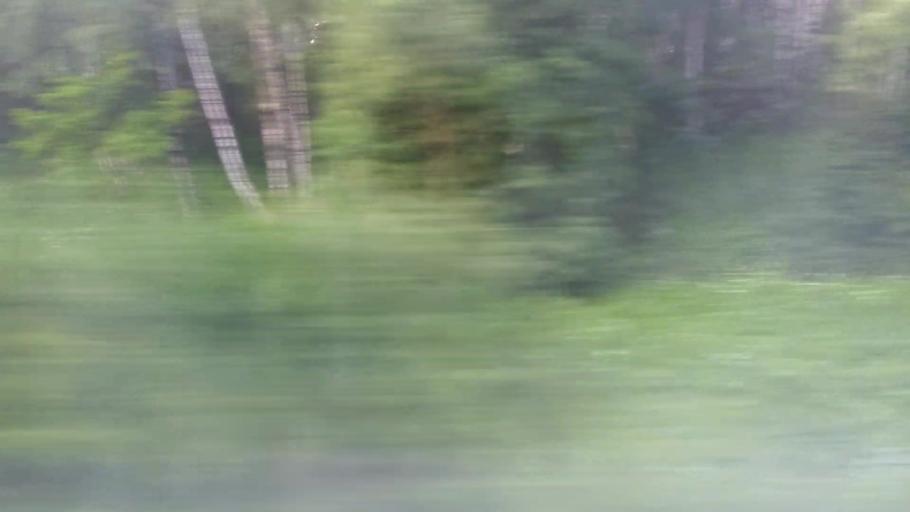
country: RU
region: Moskovskaya
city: Barybino
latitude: 55.2826
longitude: 37.8904
